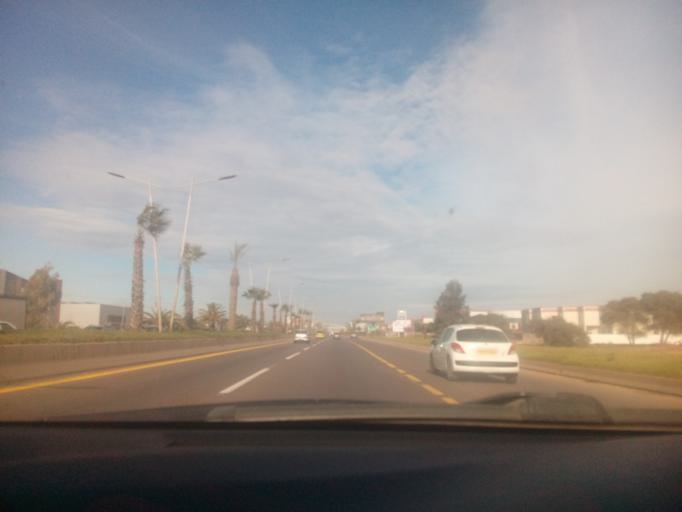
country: DZ
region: Oran
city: Es Senia
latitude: 35.6346
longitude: -0.5876
